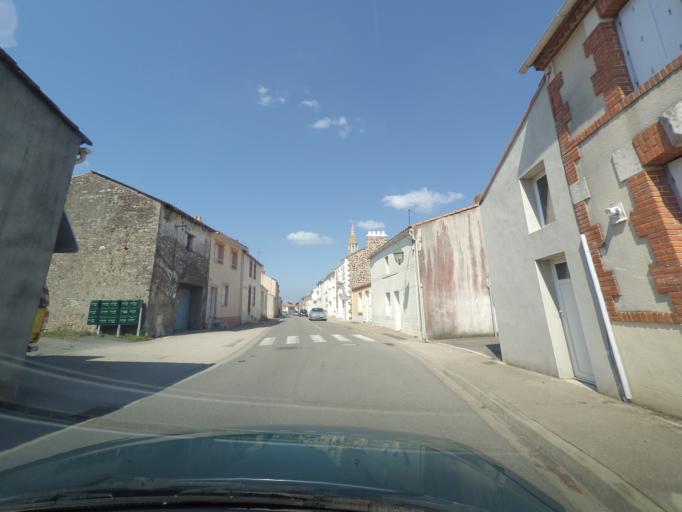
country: FR
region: Pays de la Loire
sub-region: Departement de la Loire-Atlantique
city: Saint-Lumine-de-Coutais
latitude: 47.0539
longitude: -1.7264
